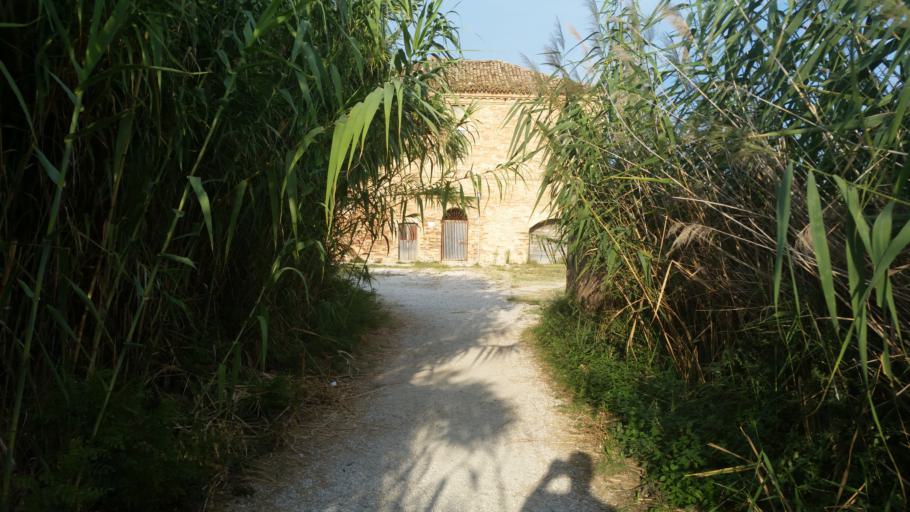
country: IT
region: Abruzzo
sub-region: Provincia di Teramo
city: Martinsicuro
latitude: 42.9033
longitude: 13.9090
